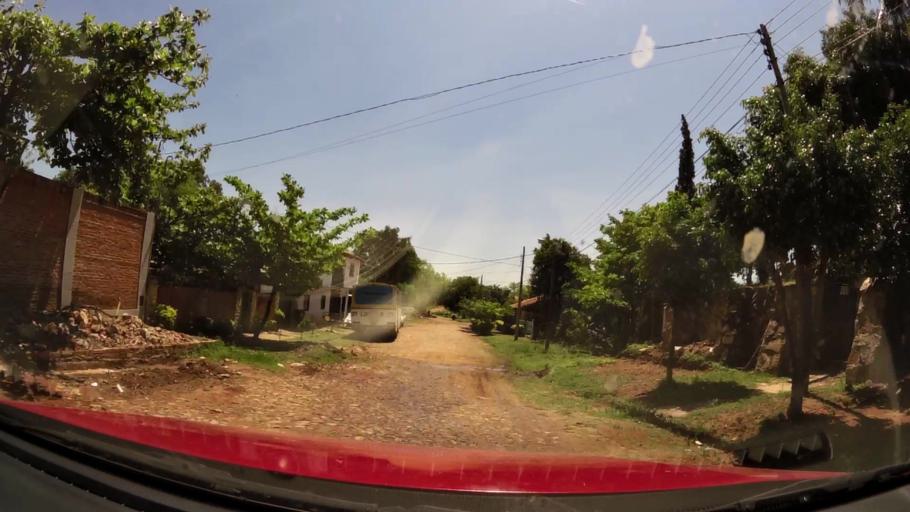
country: PY
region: Central
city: Colonia Mariano Roque Alonso
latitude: -25.2397
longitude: -57.5504
